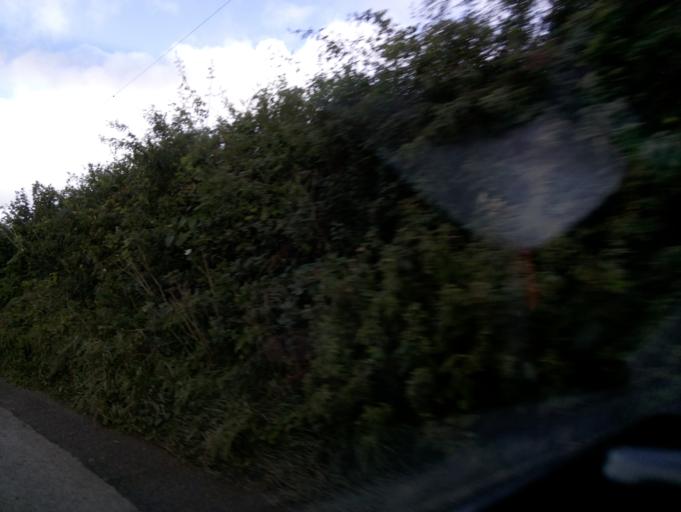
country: GB
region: England
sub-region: Devon
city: Kingsbridge
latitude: 50.3007
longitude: -3.7902
